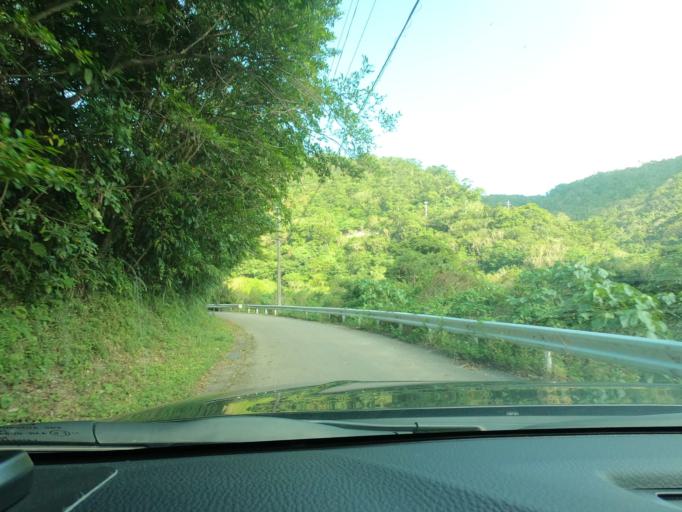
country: JP
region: Okinawa
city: Nago
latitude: 26.7639
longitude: 128.2159
